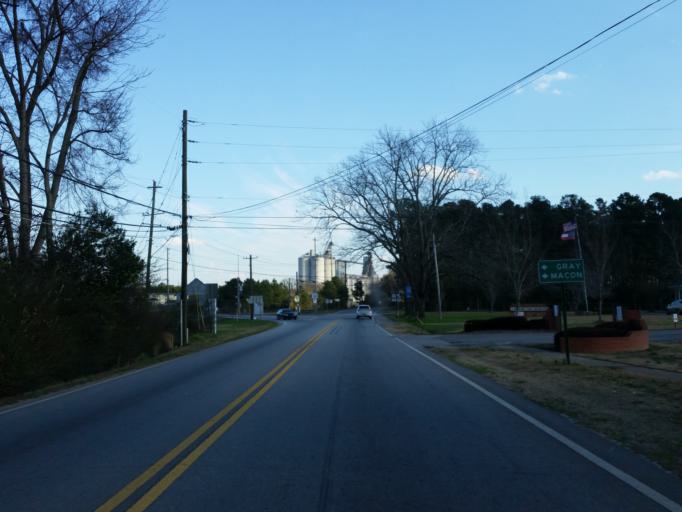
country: US
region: Georgia
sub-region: Monroe County
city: Forsyth
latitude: 33.0269
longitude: -83.9233
